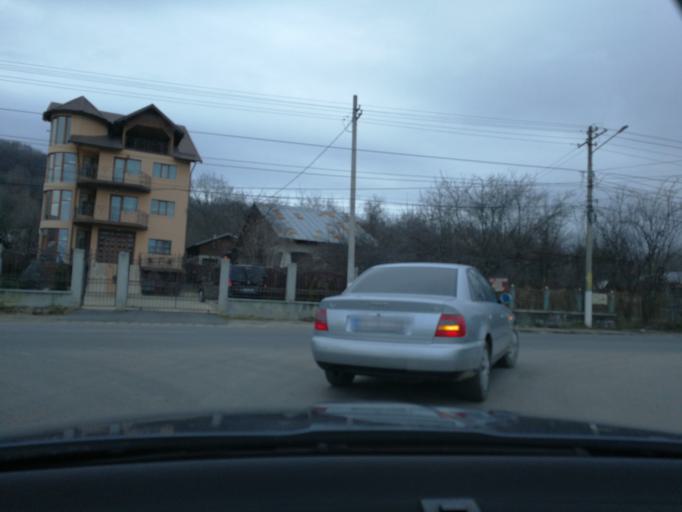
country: RO
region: Prahova
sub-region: Comuna Poiana Campina
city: Poiana Campina
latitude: 45.1438
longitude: 25.6938
